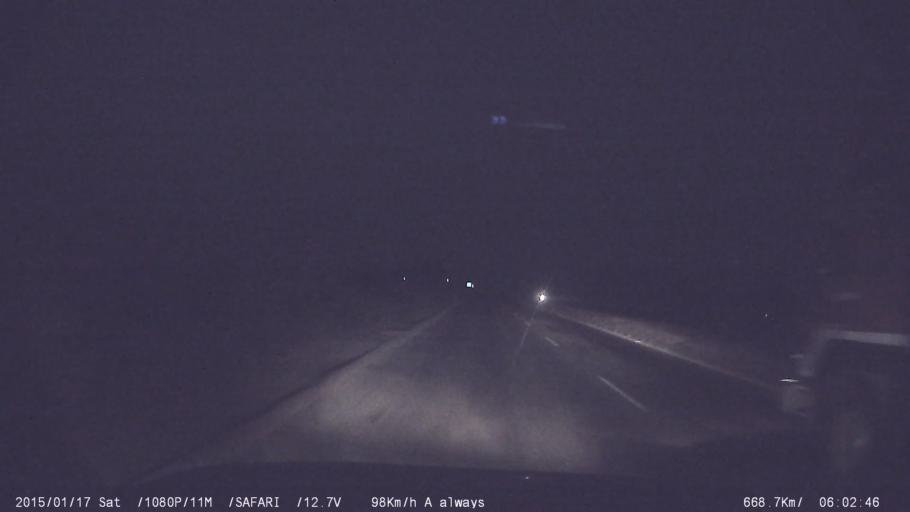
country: IN
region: Tamil Nadu
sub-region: Kancheepuram
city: Kanchipuram
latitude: 12.8874
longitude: 79.5961
